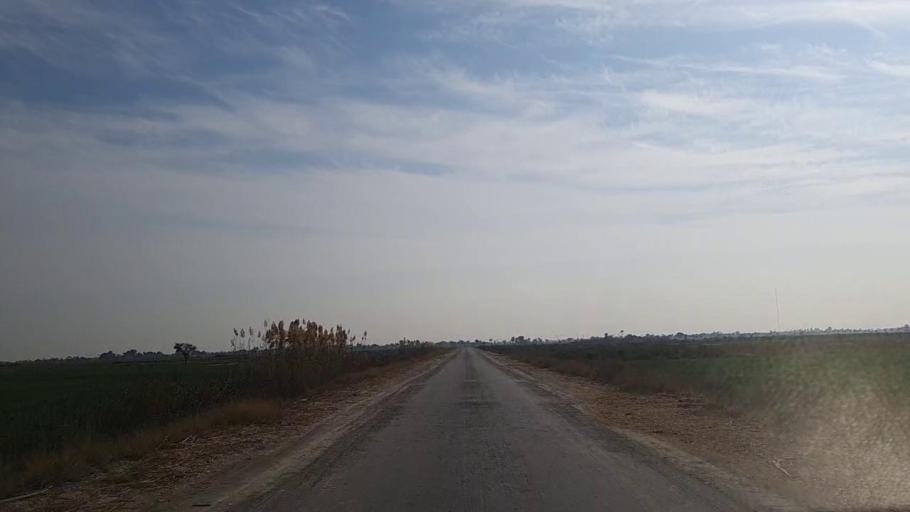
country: PK
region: Sindh
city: Daur
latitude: 26.4814
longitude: 68.4128
